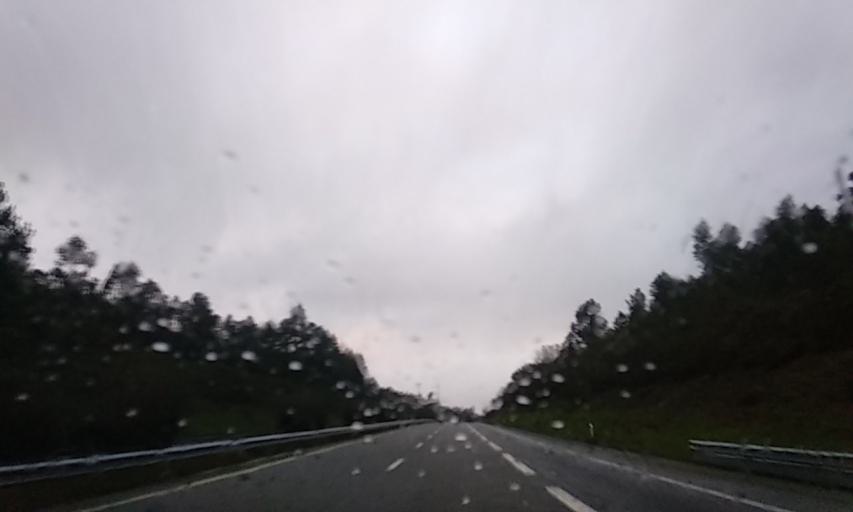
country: PT
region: Braga
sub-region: Barcelos
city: Galegos
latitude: 41.5945
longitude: -8.5532
